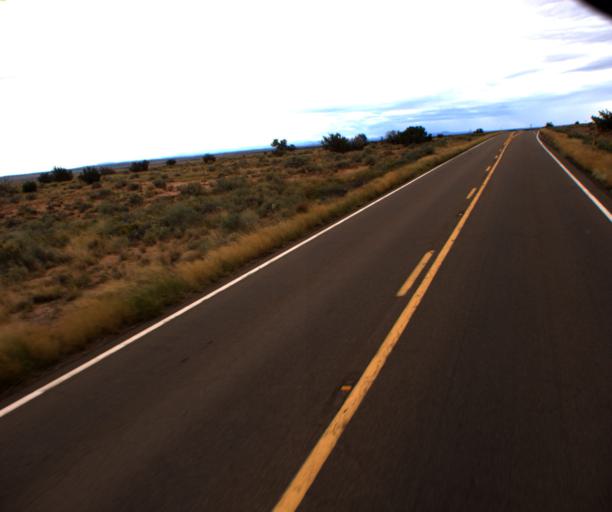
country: US
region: Arizona
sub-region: Navajo County
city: Snowflake
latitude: 34.6804
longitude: -110.1039
